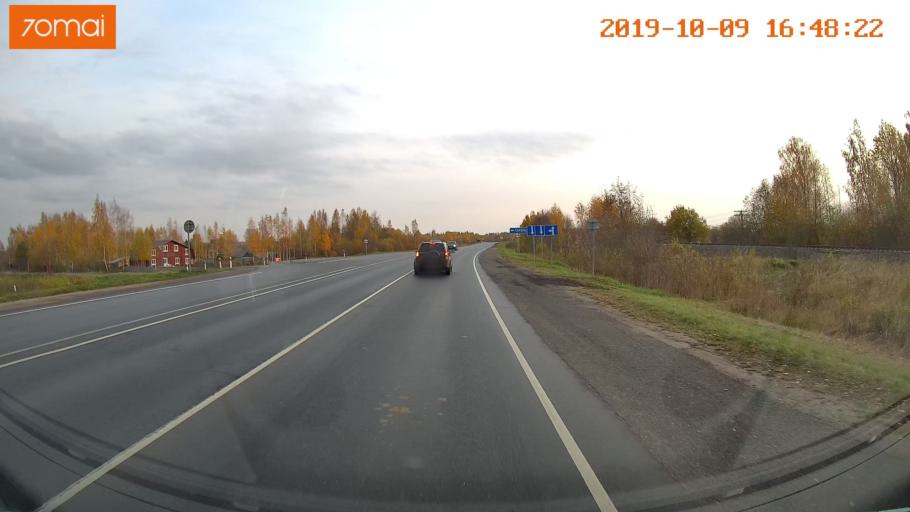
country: RU
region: Kostroma
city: Volgorechensk
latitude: 57.4282
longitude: 41.1902
